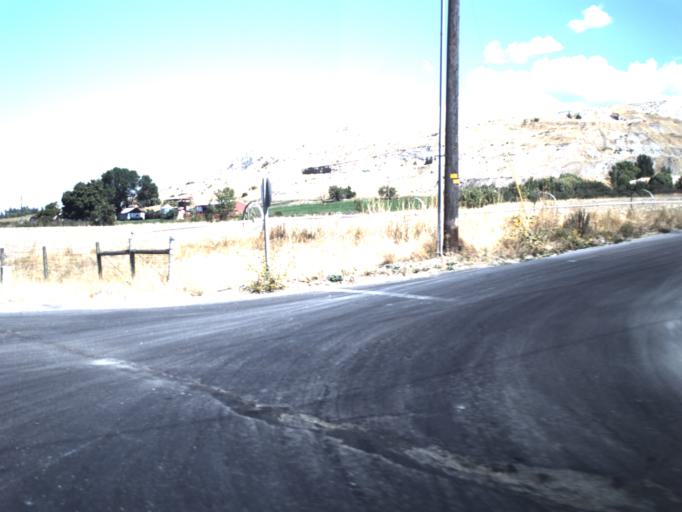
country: US
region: Utah
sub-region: Cache County
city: Smithfield
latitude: 41.8529
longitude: -111.8317
